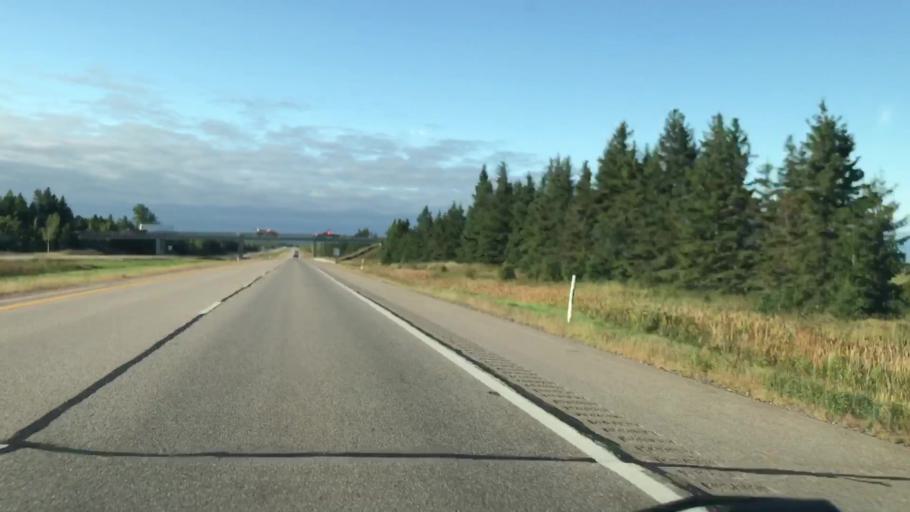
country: US
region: Michigan
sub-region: Chippewa County
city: Sault Ste. Marie
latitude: 46.4217
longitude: -84.3942
